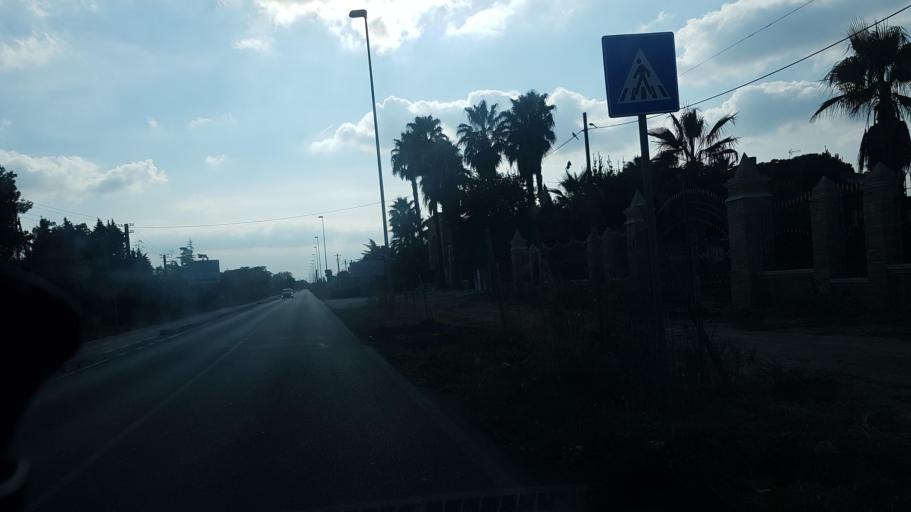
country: IT
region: Apulia
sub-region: Provincia di Foggia
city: Foggia
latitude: 41.4430
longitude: 15.5254
